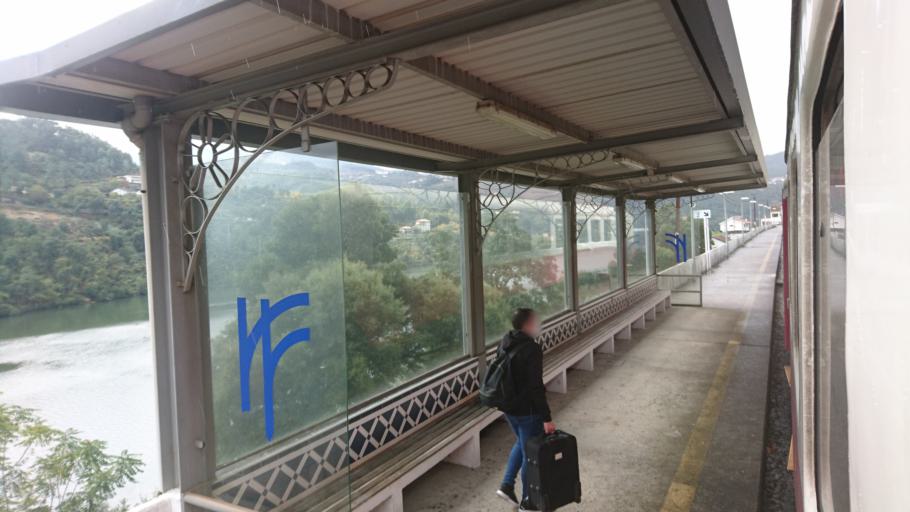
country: PT
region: Viseu
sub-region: Cinfaes
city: Cinfaes
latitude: 41.0946
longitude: -8.0686
